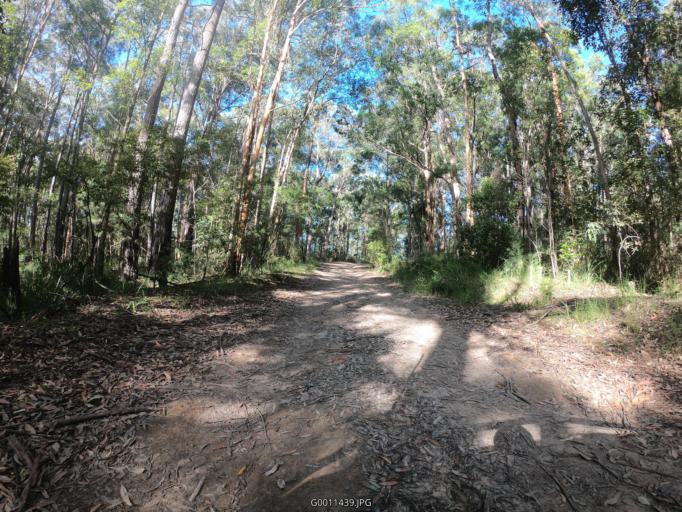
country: AU
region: New South Wales
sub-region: Lake Macquarie Shire
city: Cooranbong
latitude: -33.0277
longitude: 151.3054
